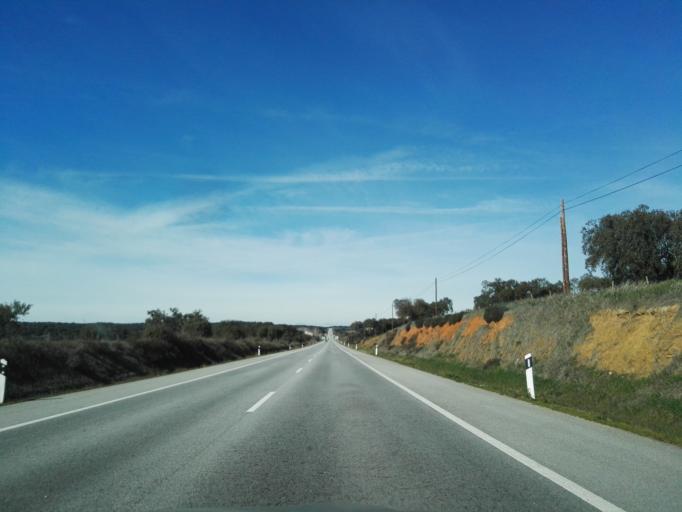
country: PT
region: Portalegre
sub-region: Arronches
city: Arronches
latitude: 39.1546
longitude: -7.3149
